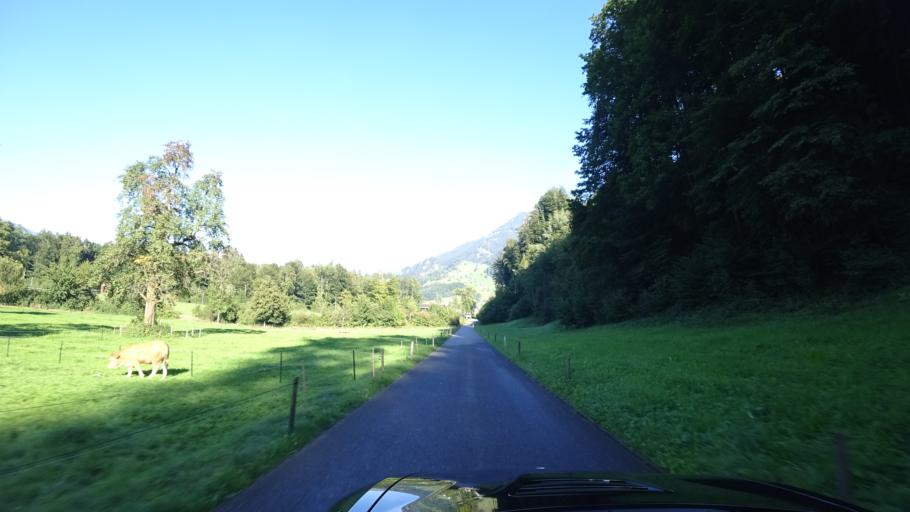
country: CH
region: Obwalden
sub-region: Obwalden
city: Giswil
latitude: 46.8292
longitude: 8.1641
